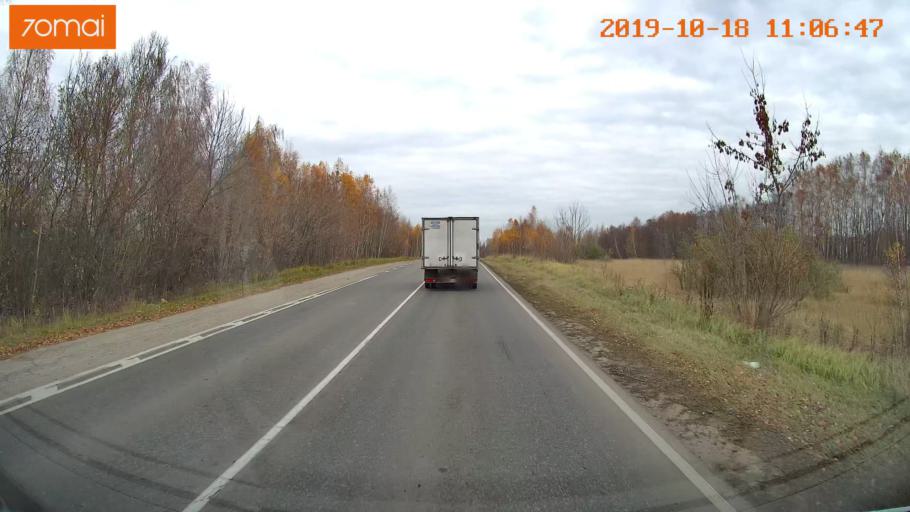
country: RU
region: Tula
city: Kimovsk
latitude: 53.9214
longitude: 38.5348
